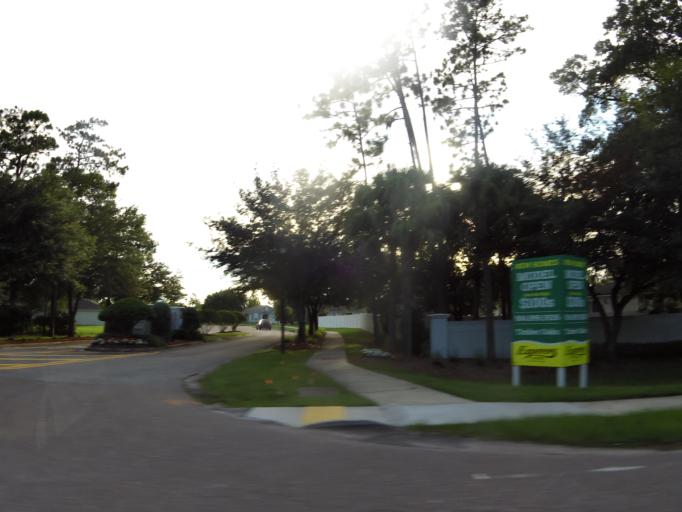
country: US
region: Florida
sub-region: Duval County
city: Jacksonville
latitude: 30.4104
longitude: -81.6974
